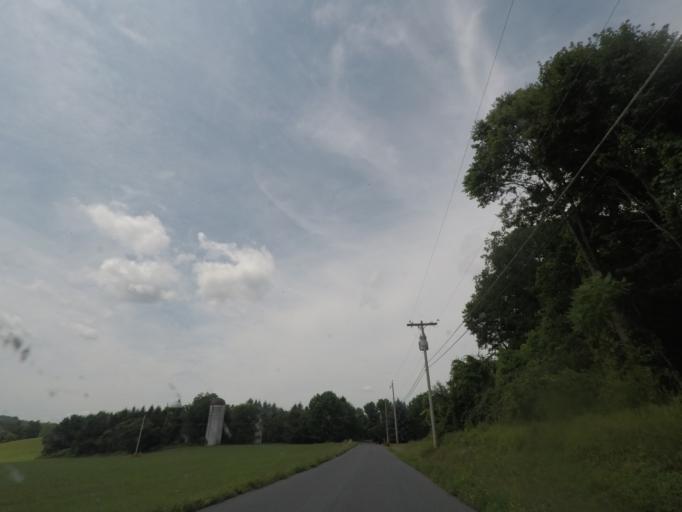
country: US
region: New York
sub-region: Rensselaer County
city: Wynantskill
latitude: 42.7133
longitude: -73.6300
